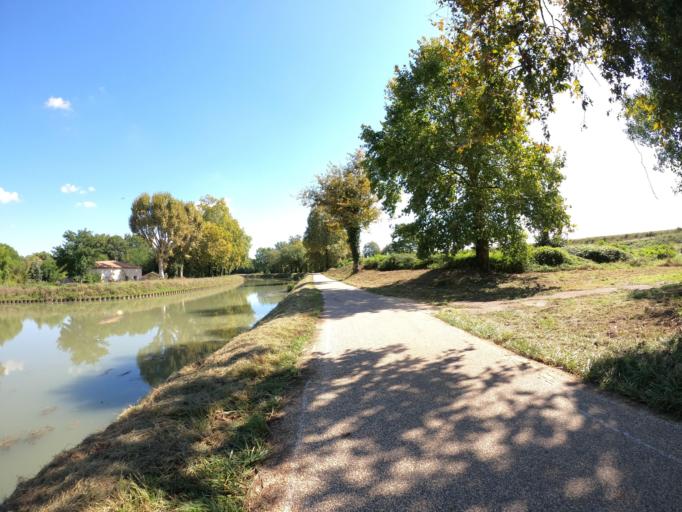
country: FR
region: Midi-Pyrenees
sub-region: Departement du Tarn-et-Garonne
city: Valence
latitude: 44.1049
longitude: 0.8884
